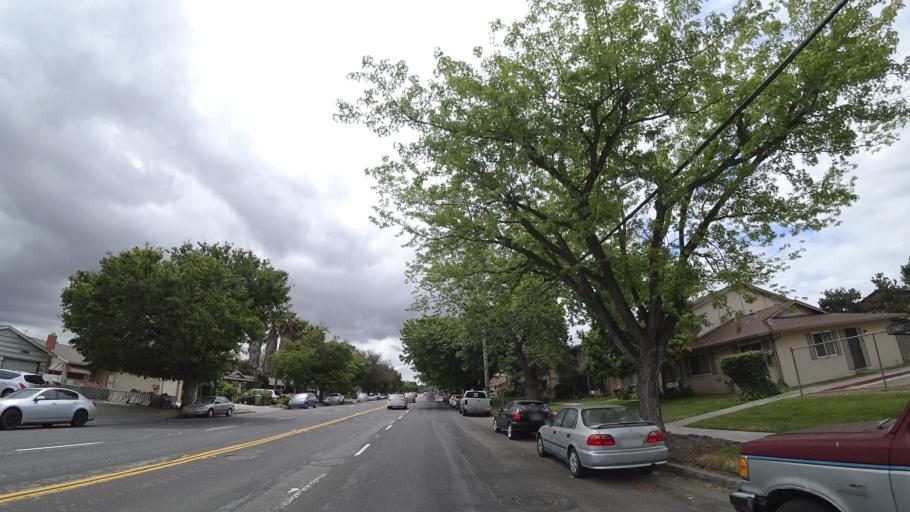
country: US
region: California
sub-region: Santa Clara County
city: Seven Trees
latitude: 37.2891
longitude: -121.8291
